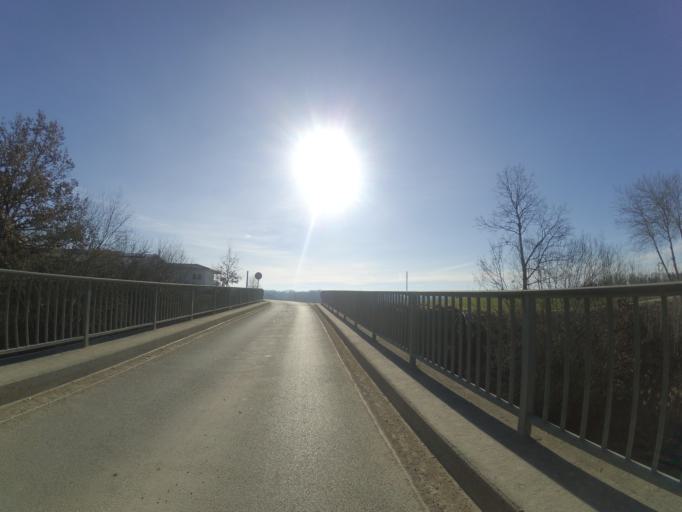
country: DE
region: Baden-Wuerttemberg
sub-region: Tuebingen Region
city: Aulendorf
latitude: 47.9375
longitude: 9.6370
